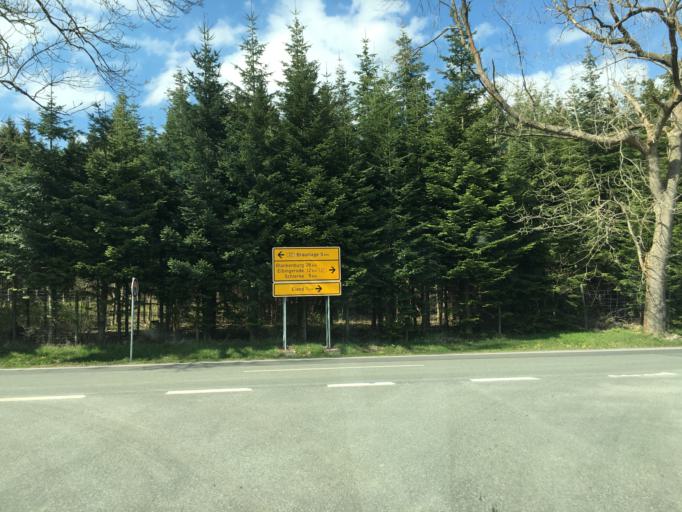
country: DE
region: Lower Saxony
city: Braunlage
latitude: 51.7392
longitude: 10.6772
